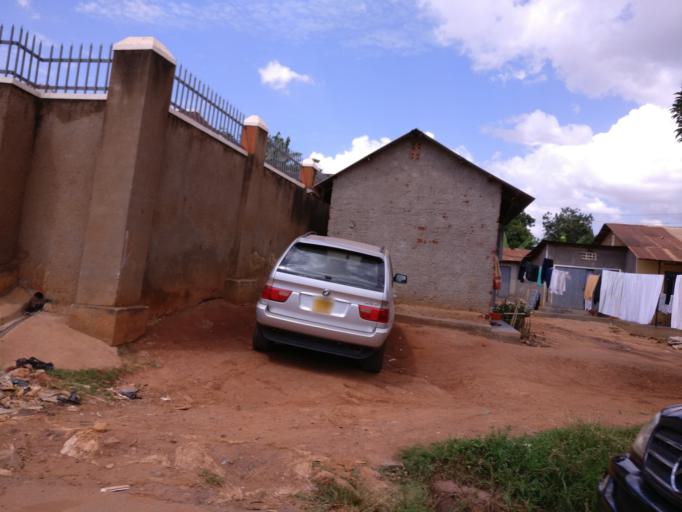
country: UG
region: Central Region
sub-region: Kampala District
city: Kampala
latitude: 0.2845
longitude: 32.5643
